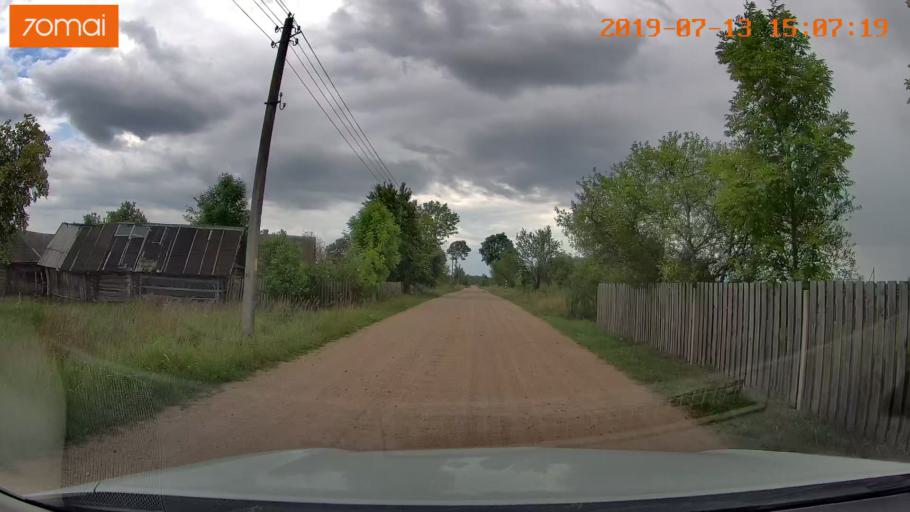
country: BY
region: Mogilev
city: Hlusha
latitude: 53.1918
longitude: 28.7567
